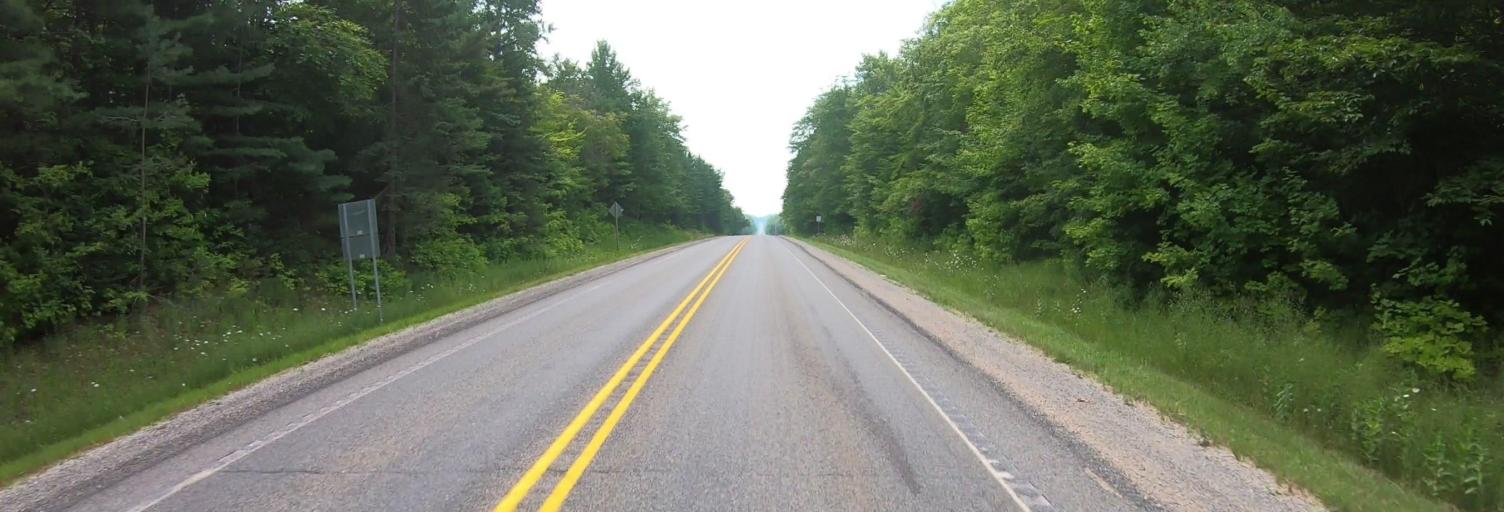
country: US
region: Michigan
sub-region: Alger County
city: Munising
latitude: 46.3753
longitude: -86.7016
